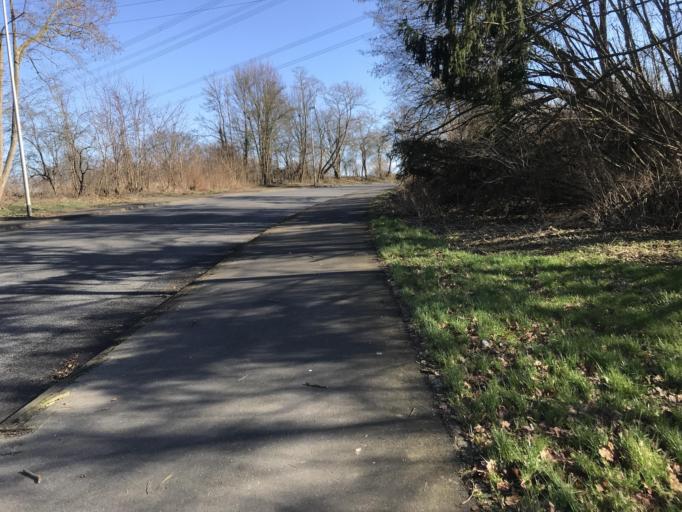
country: DE
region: Hesse
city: Schwalmstadt
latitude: 50.9081
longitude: 9.2051
